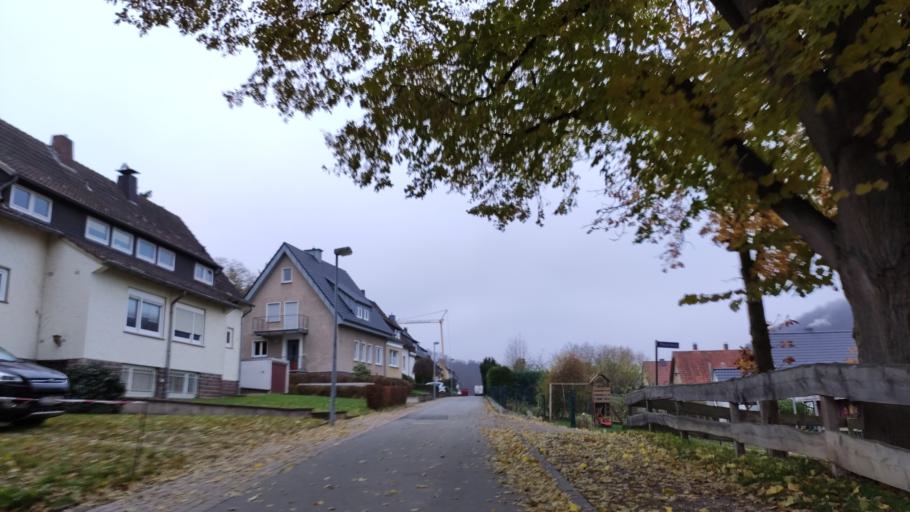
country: DE
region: North Rhine-Westphalia
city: Beverungen
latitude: 51.7030
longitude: 9.2880
